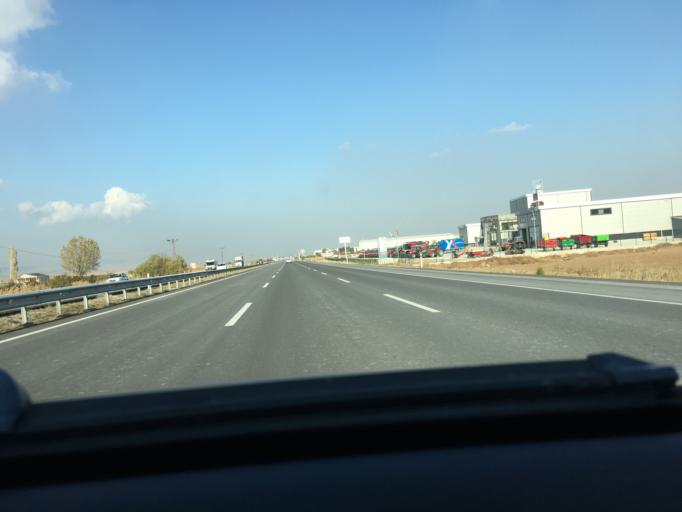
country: TR
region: Ankara
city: Polatli
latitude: 39.6396
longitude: 32.2041
